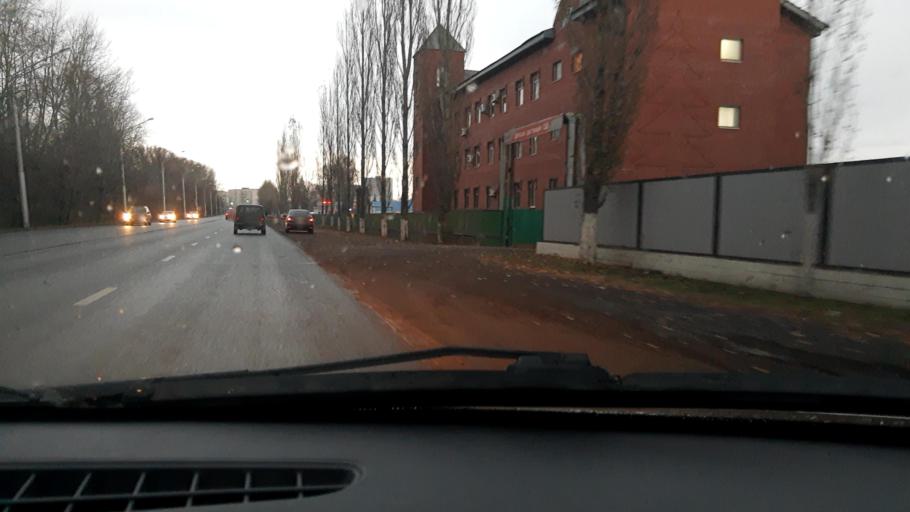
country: RU
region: Bashkortostan
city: Avdon
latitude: 54.6861
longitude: 55.8149
